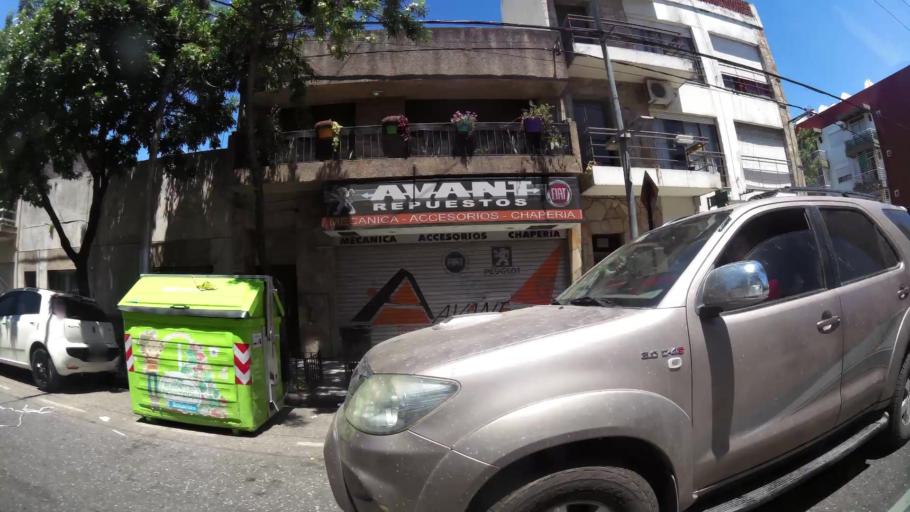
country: AR
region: Santa Fe
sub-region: Departamento de Rosario
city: Rosario
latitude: -32.9435
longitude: -60.6844
